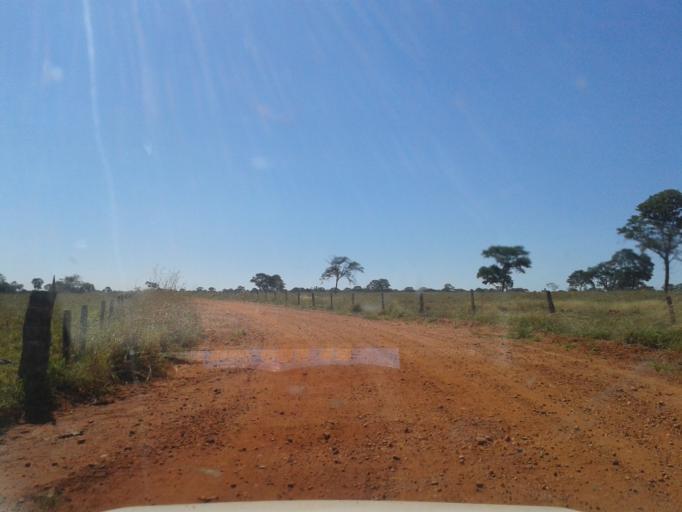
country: BR
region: Minas Gerais
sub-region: Santa Vitoria
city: Santa Vitoria
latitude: -19.0770
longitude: -50.3596
